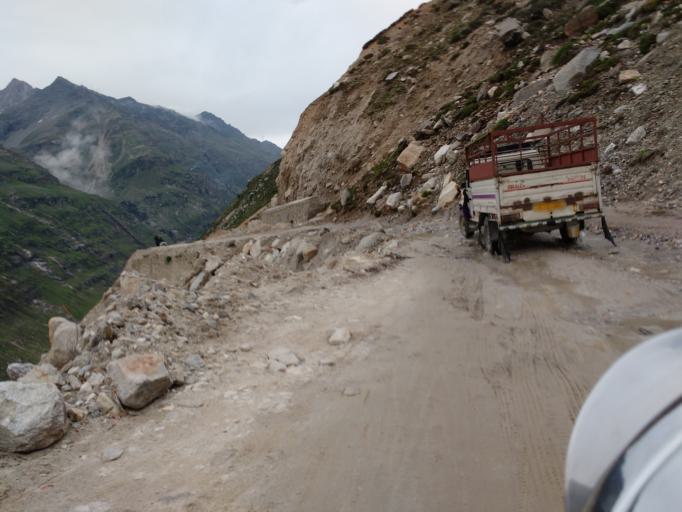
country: IN
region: Himachal Pradesh
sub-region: Kulu
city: Manali
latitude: 32.3787
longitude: 77.2671
